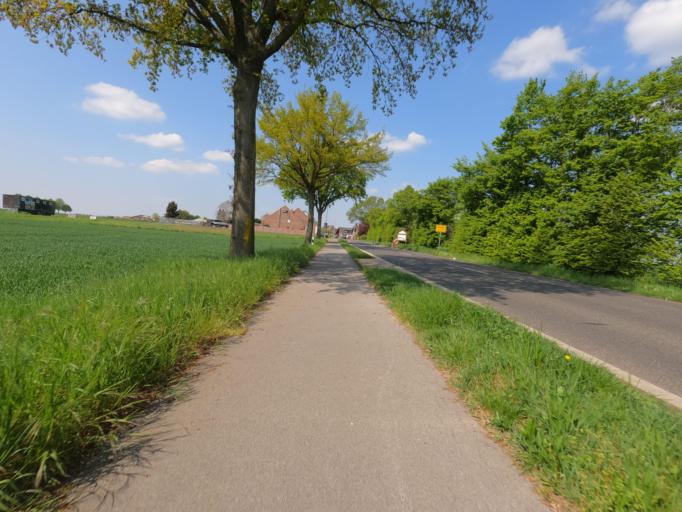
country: DE
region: North Rhine-Westphalia
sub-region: Regierungsbezirk Koln
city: Heinsberg
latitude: 51.0261
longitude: 6.0827
